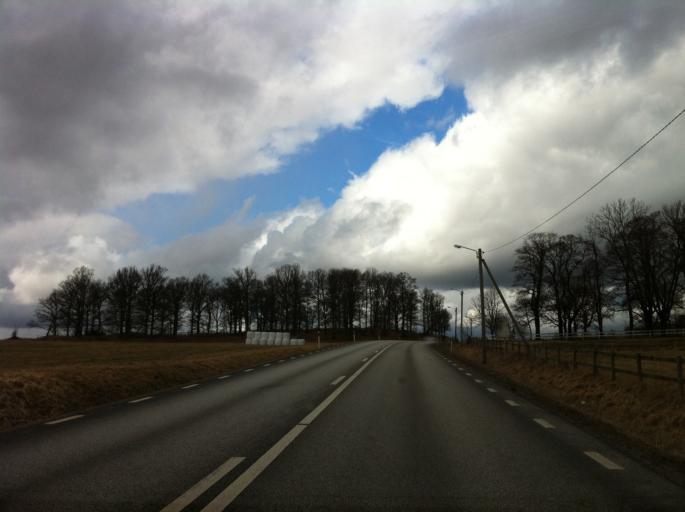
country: SE
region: Vaestra Goetaland
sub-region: Ulricehamns Kommun
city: Ulricehamn
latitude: 57.6572
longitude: 13.4332
